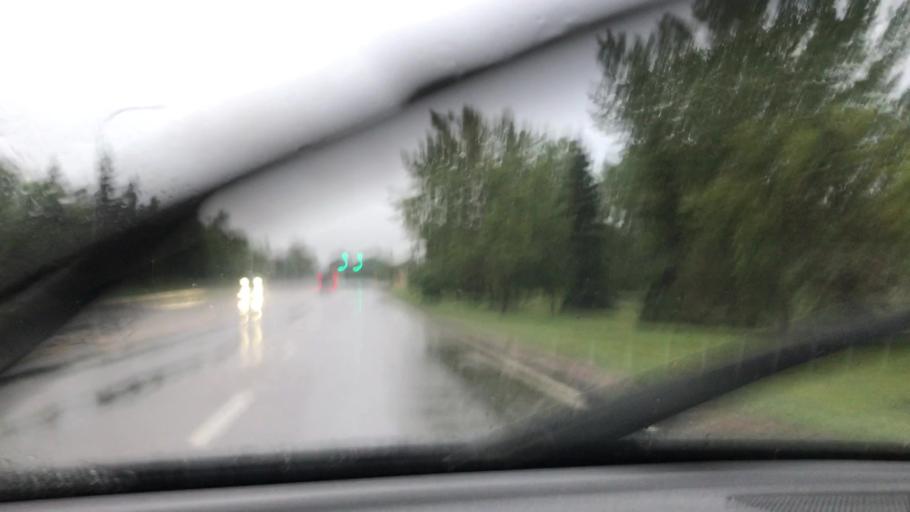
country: CA
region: Alberta
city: Sherwood Park
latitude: 53.5219
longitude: -113.3161
